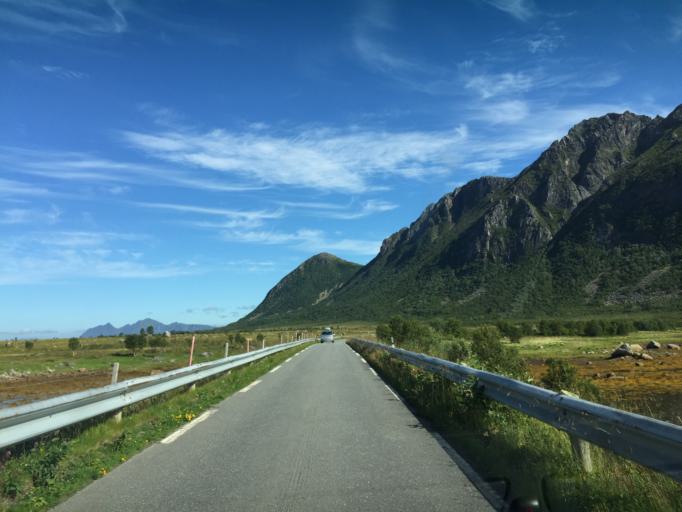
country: NO
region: Nordland
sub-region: Vagan
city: Svolvaer
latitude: 68.3972
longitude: 14.5648
